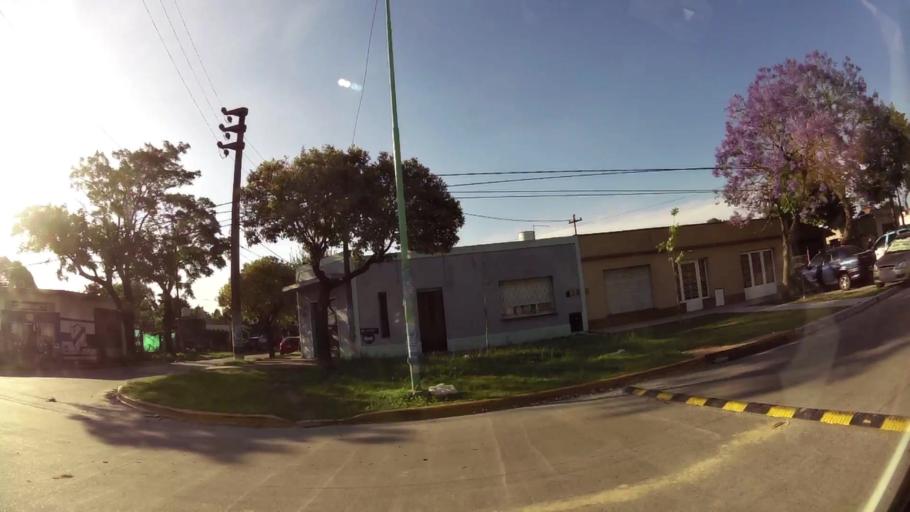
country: AR
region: Buenos Aires
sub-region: Partido de Merlo
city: Merlo
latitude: -34.6805
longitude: -58.7296
